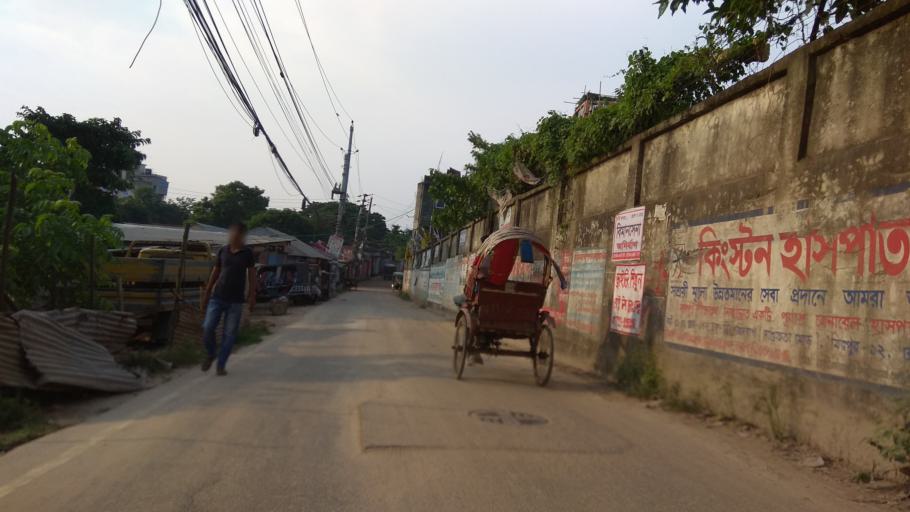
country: BD
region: Dhaka
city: Tungi
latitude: 23.8410
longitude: 90.3874
